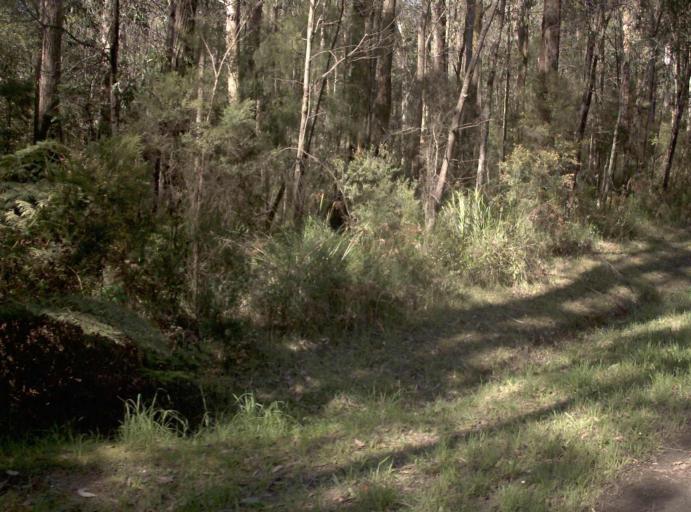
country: AU
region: Victoria
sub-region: Yarra Ranges
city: Millgrove
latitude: -37.8847
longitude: 145.8861
